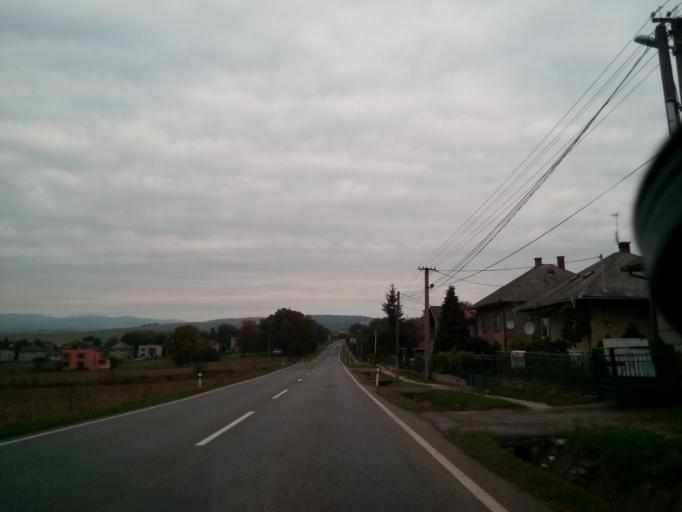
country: SK
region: Presovsky
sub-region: Okres Presov
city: Presov
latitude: 49.0847
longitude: 21.3154
